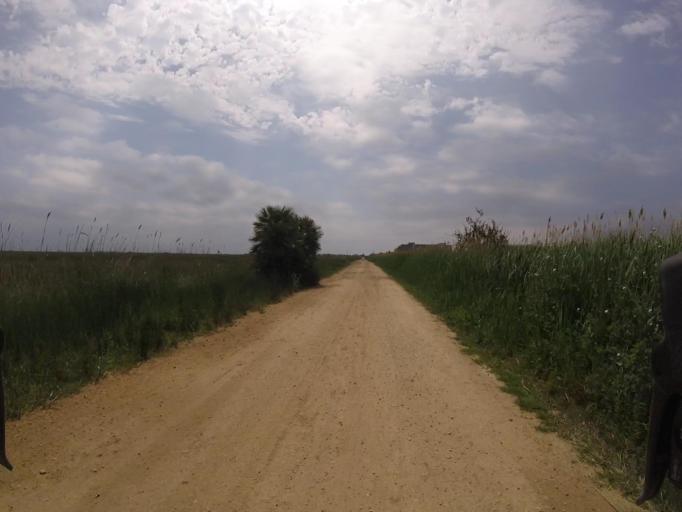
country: ES
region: Valencia
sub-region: Provincia de Castello
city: Orpesa/Oropesa del Mar
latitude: 40.1417
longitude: 0.1639
